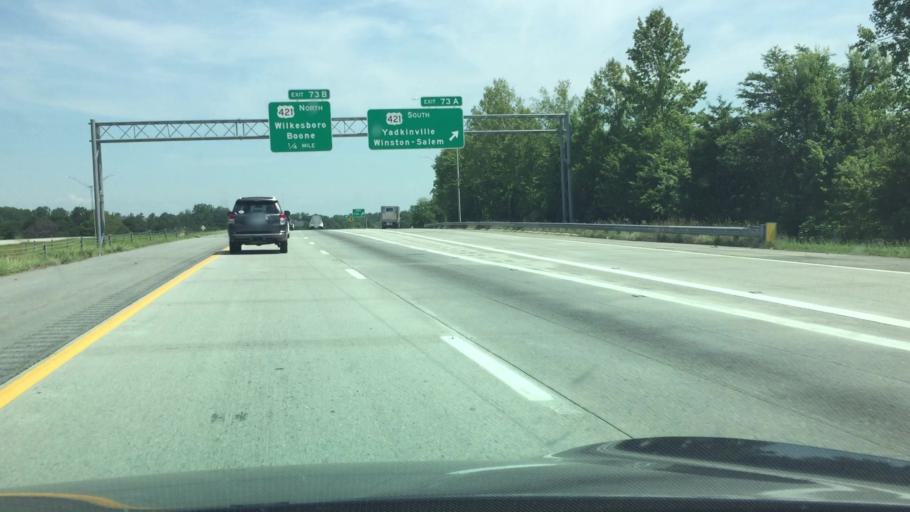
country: US
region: North Carolina
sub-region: Yadkin County
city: Jonesville
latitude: 36.1172
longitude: -80.8142
